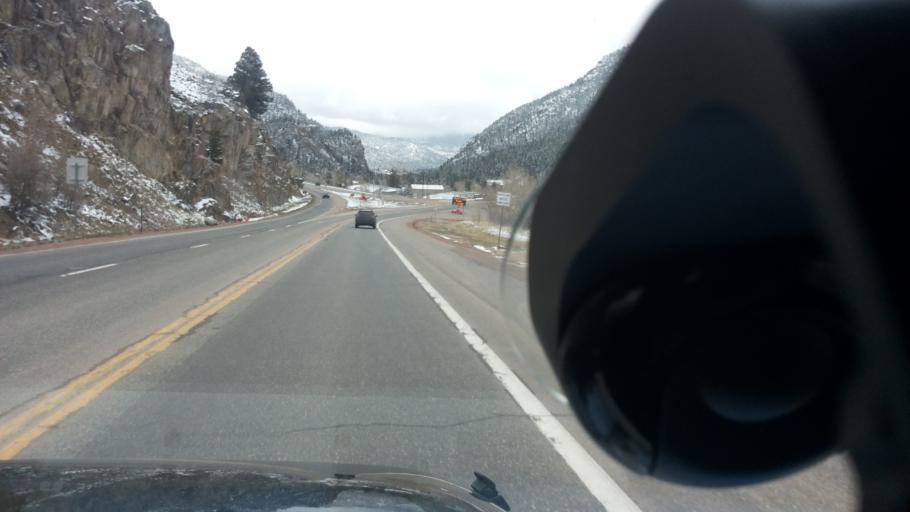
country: US
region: Colorado
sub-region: Clear Creek County
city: Georgetown
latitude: 39.7596
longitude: -105.6622
